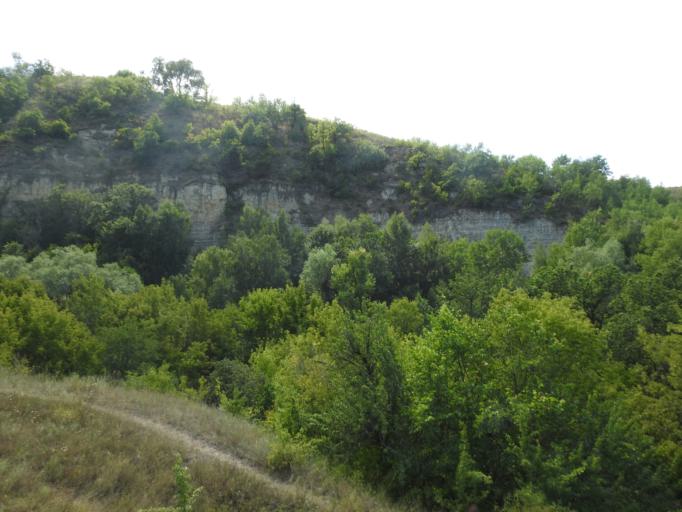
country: RU
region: Saratov
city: Kamenskiy
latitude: 50.4927
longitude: 45.7016
